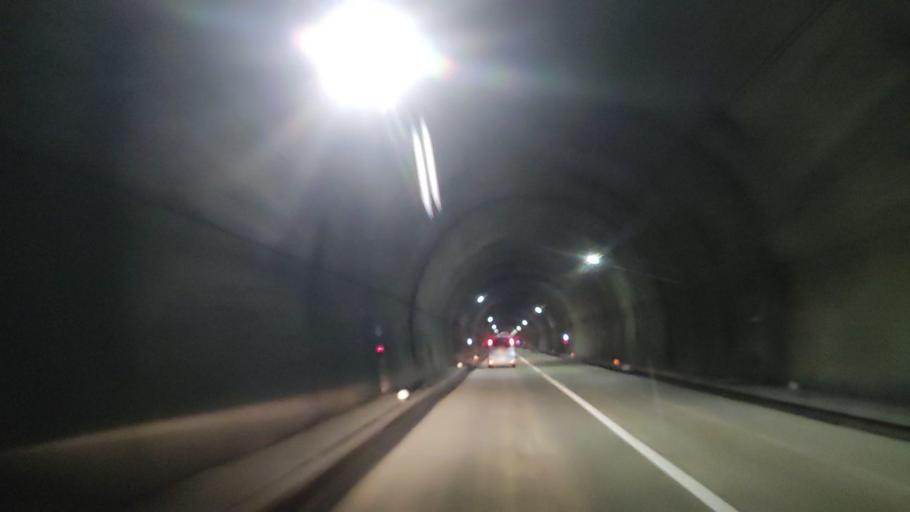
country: JP
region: Gifu
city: Takayama
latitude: 36.1818
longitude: 137.5289
